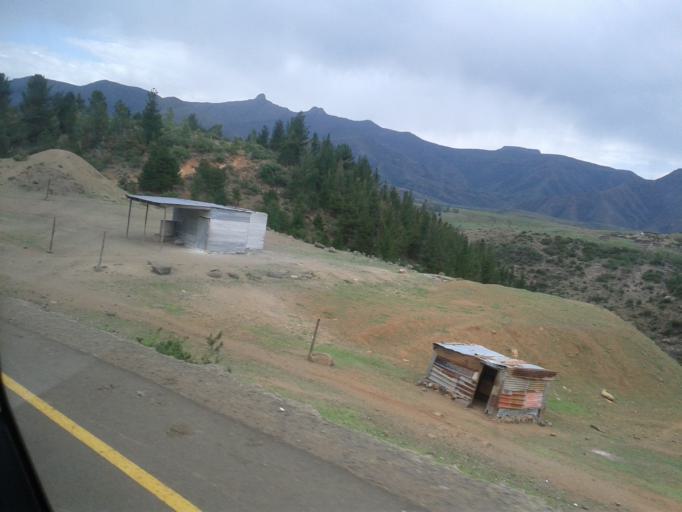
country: LS
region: Maseru
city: Nako
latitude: -29.6555
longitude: 27.8324
